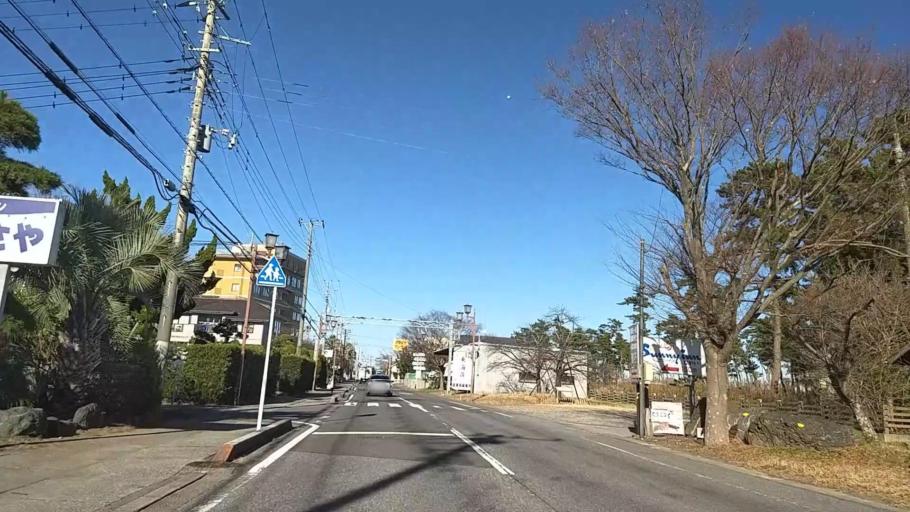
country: JP
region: Chiba
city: Mobara
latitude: 35.4295
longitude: 140.3959
